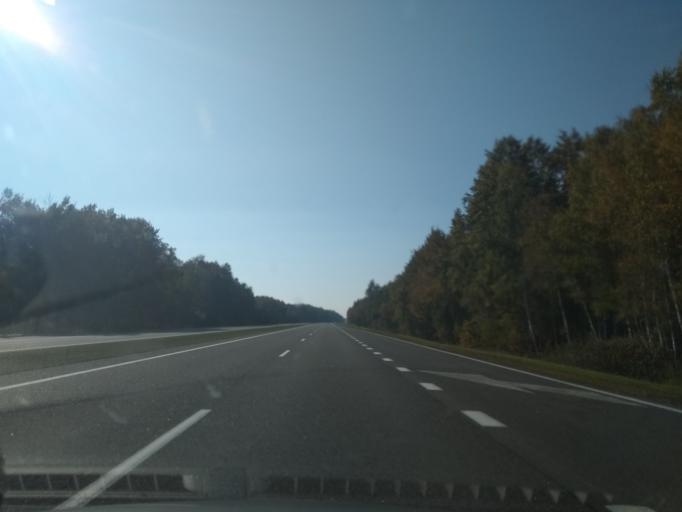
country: BY
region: Brest
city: Horad Kobryn
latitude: 52.2747
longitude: 24.5402
